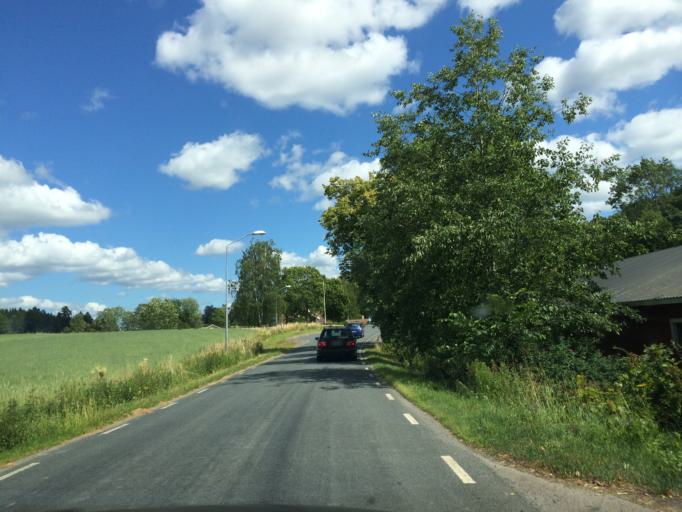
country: SE
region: Soedermanland
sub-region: Katrineholms Kommun
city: Katrineholm
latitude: 59.0670
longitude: 16.3565
